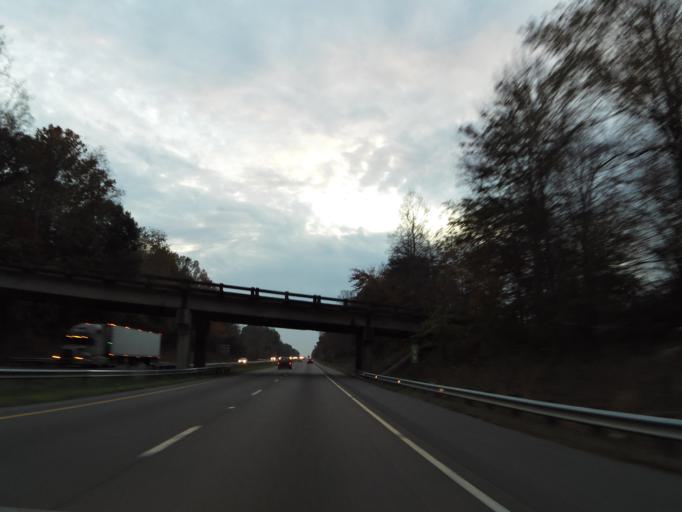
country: US
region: North Carolina
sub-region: Burke County
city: Glen Alpine
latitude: 35.7157
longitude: -81.7646
